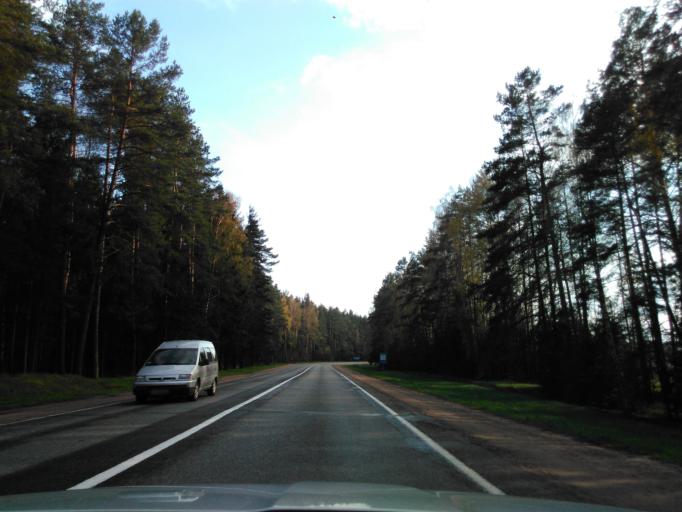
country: BY
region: Minsk
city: Lahoysk
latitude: 54.2501
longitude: 27.8504
